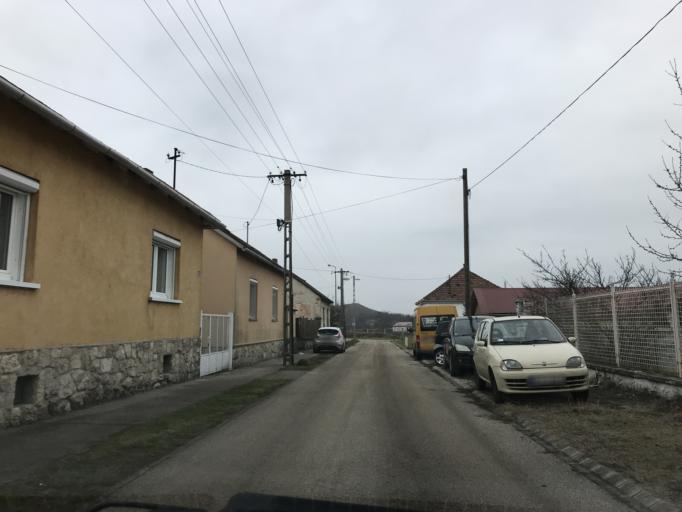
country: HU
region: Komarom-Esztergom
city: Tokod
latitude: 47.7281
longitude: 18.6623
